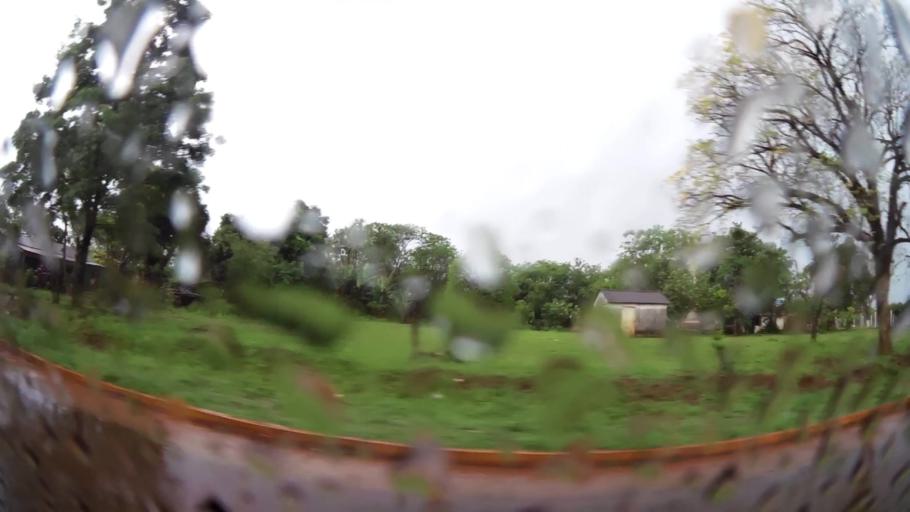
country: PY
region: Alto Parana
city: Presidente Franco
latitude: -25.5504
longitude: -54.6702
